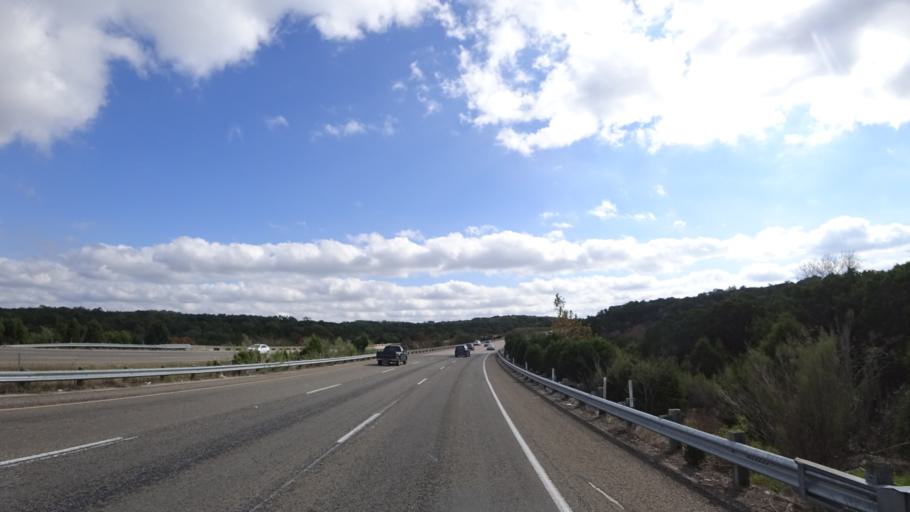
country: US
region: Texas
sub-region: Travis County
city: Barton Creek
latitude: 30.2797
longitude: -97.9021
